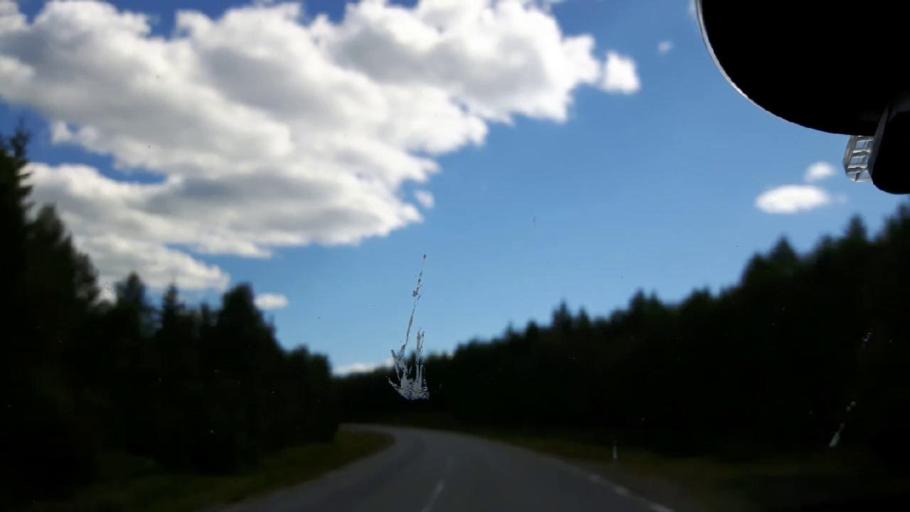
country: SE
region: Vaesternorrland
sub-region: Ange Kommun
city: Fransta
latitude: 62.8221
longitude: 16.1946
